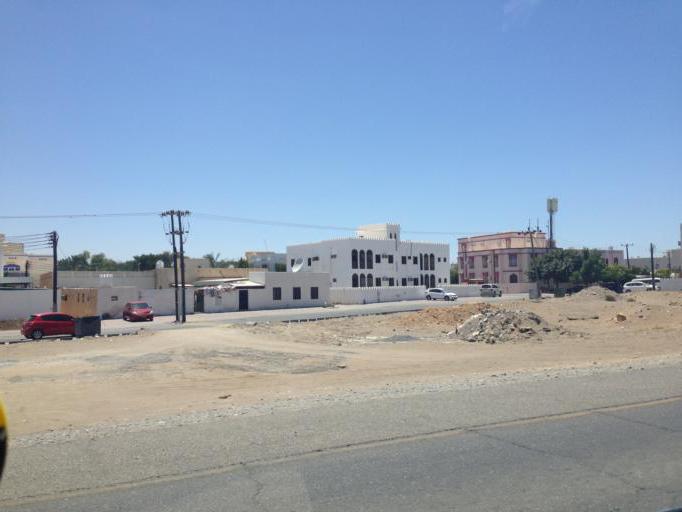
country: OM
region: Muhafazat Masqat
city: As Sib al Jadidah
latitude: 23.6555
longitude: 58.2228
